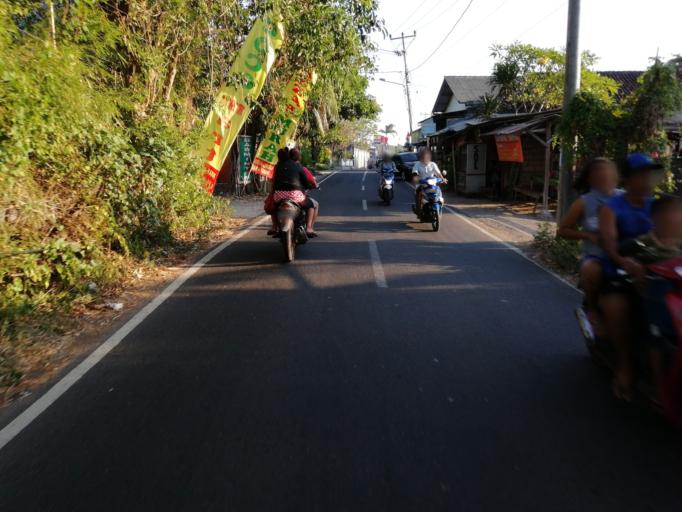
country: ID
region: Bali
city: Bualu
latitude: -8.7876
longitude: 115.1969
